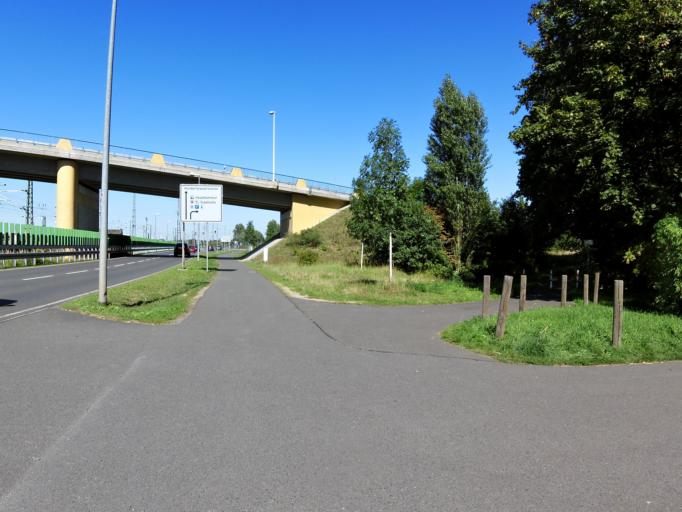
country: DE
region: Saxony-Anhalt
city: Wittenburg
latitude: 51.8655
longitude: 12.6609
